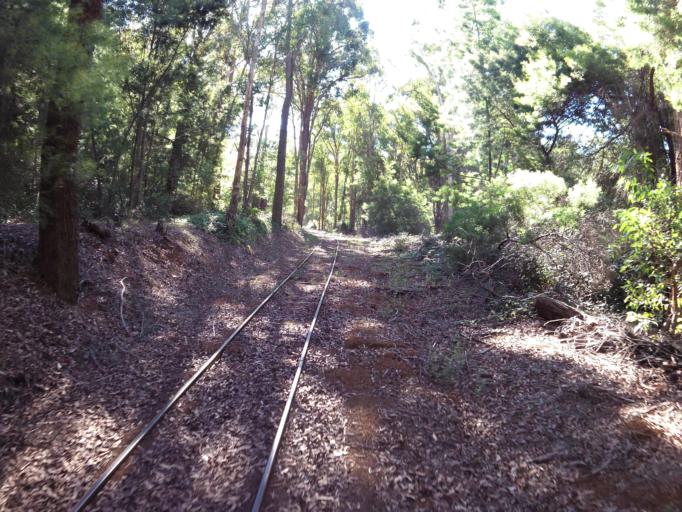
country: AU
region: Western Australia
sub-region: Waroona
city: Waroona
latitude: -32.7168
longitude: 116.0972
